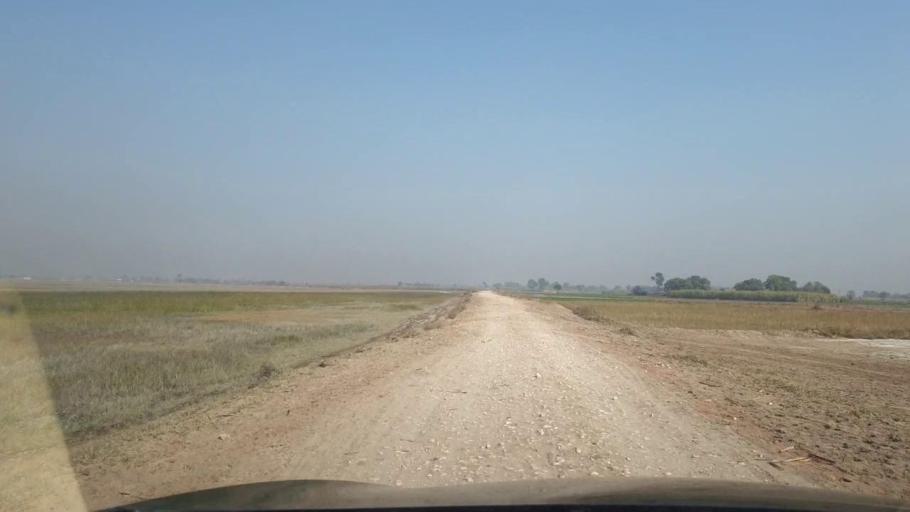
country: PK
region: Sindh
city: Ubauro
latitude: 28.1265
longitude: 69.7492
